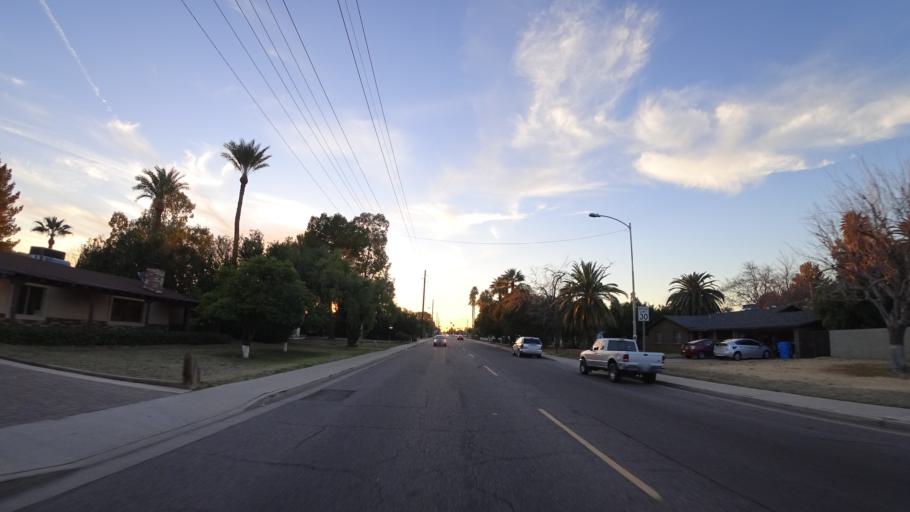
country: US
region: Arizona
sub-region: Maricopa County
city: Tempe Junction
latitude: 33.4730
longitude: -111.9926
